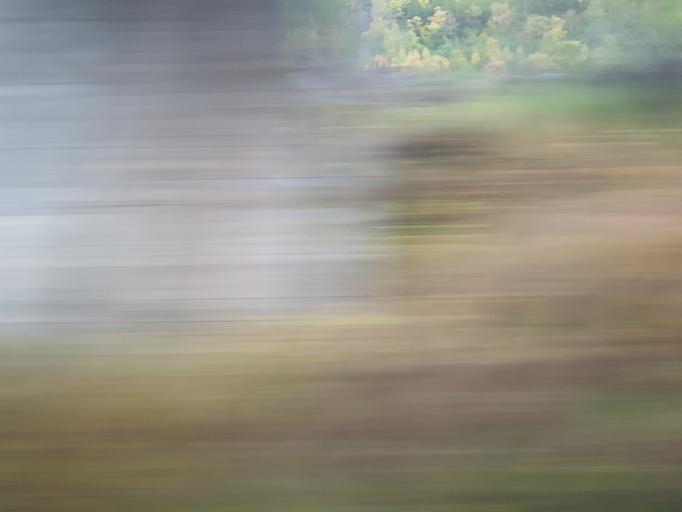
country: NO
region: Oppland
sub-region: Sel
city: Otta
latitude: 61.8396
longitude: 9.4695
